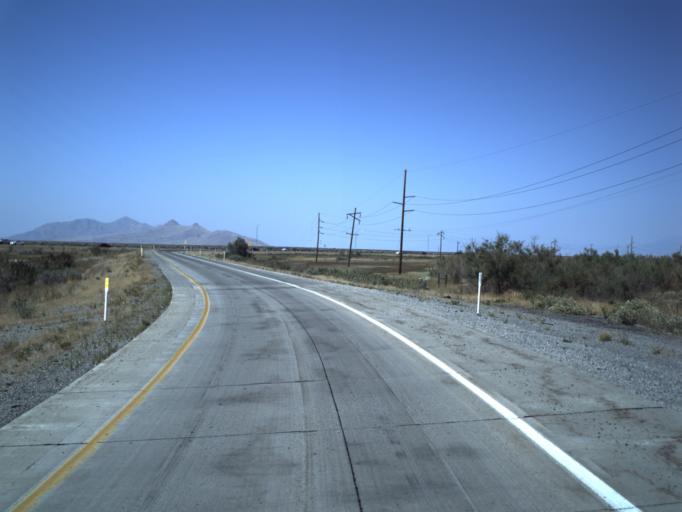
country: US
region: Utah
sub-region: Salt Lake County
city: Magna
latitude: 40.7450
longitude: -112.1791
